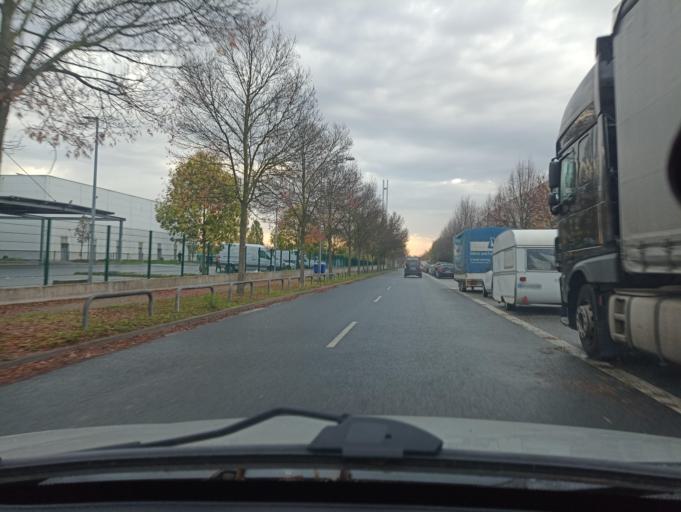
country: DE
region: Hesse
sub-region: Regierungsbezirk Darmstadt
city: Bad Homburg vor der Hoehe
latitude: 50.1960
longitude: 8.6456
